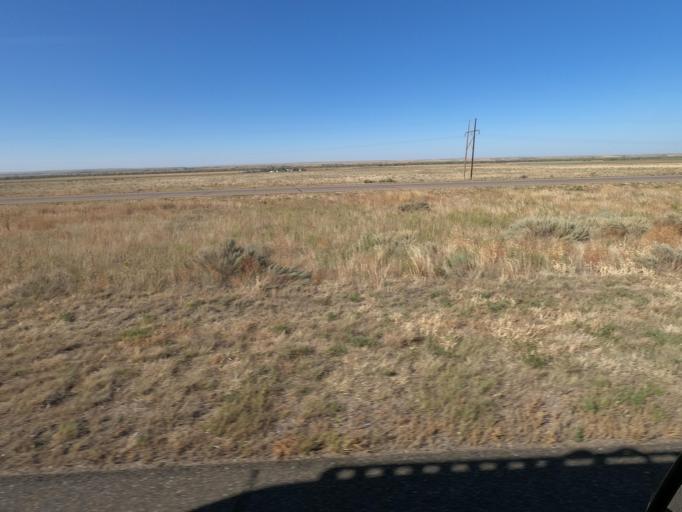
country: US
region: Nebraska
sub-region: Deuel County
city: Chappell
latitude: 40.8879
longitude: -102.5690
